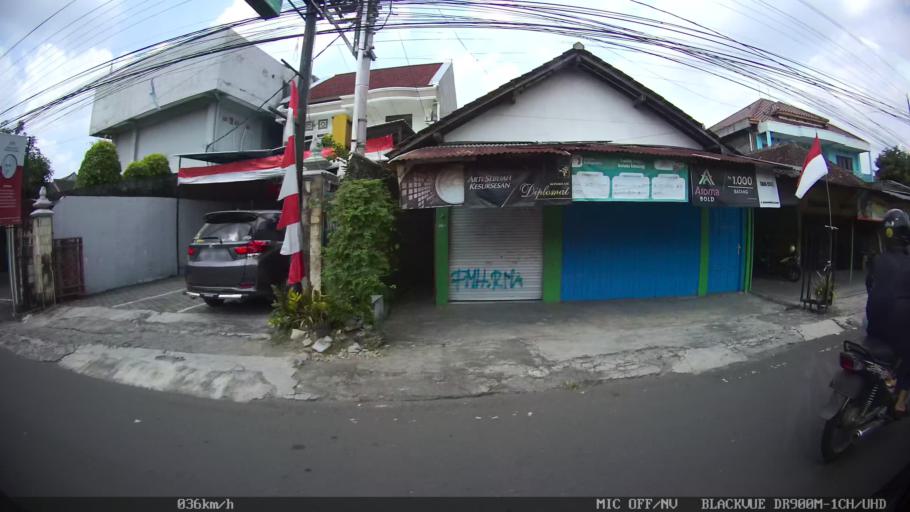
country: ID
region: Daerah Istimewa Yogyakarta
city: Yogyakarta
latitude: -7.8139
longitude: 110.4022
